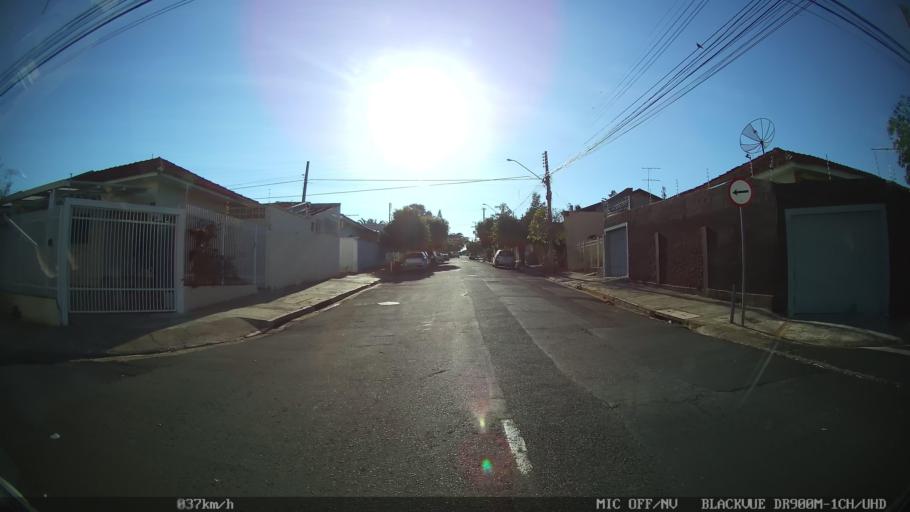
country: BR
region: Sao Paulo
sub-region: Sao Jose Do Rio Preto
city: Sao Jose do Rio Preto
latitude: -20.8139
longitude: -49.3929
